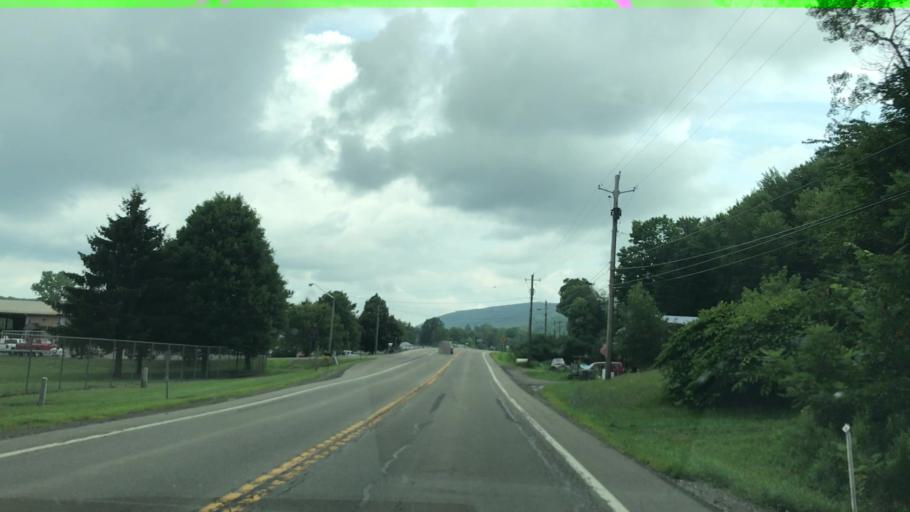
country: US
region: New York
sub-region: Steuben County
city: Bath
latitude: 42.3841
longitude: -77.3587
